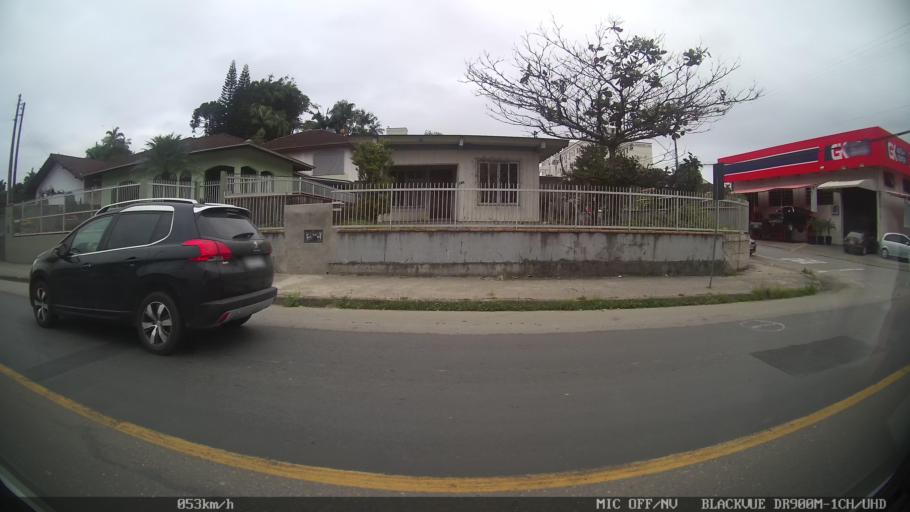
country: BR
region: Santa Catarina
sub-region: Joinville
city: Joinville
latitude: -26.2847
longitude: -48.8782
